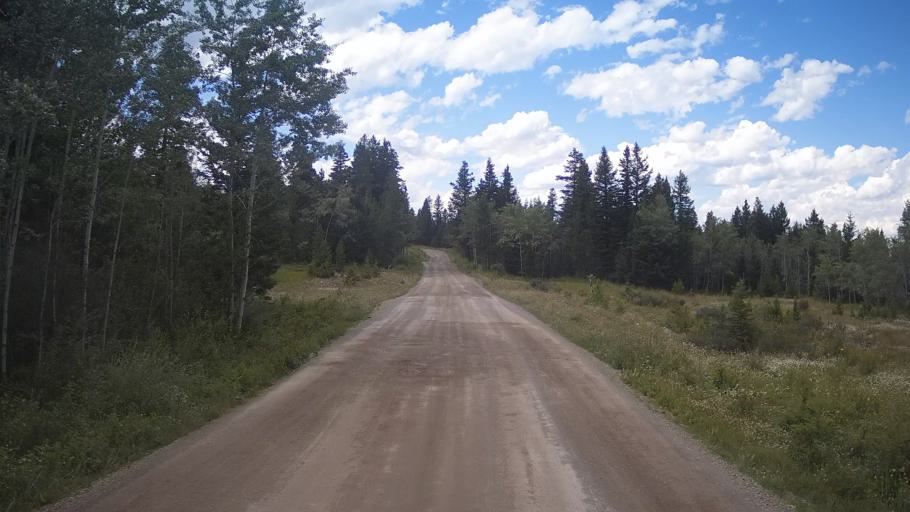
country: CA
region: British Columbia
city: Lillooet
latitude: 51.3110
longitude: -121.8458
